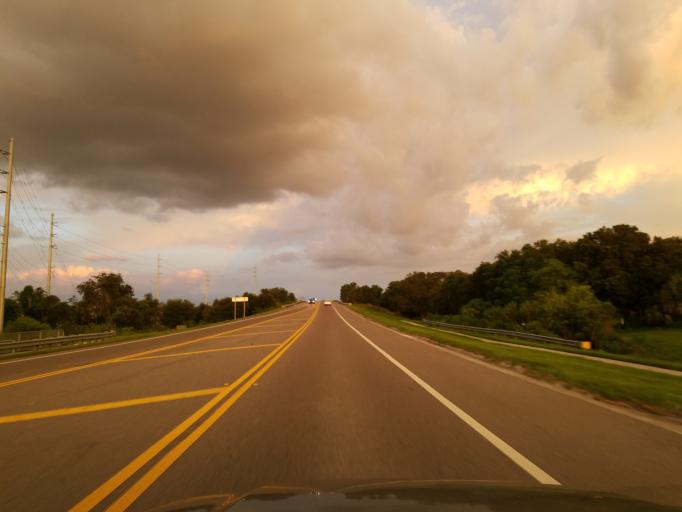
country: US
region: Florida
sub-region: Hillsborough County
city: Progress Village
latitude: 27.8971
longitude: -82.3507
